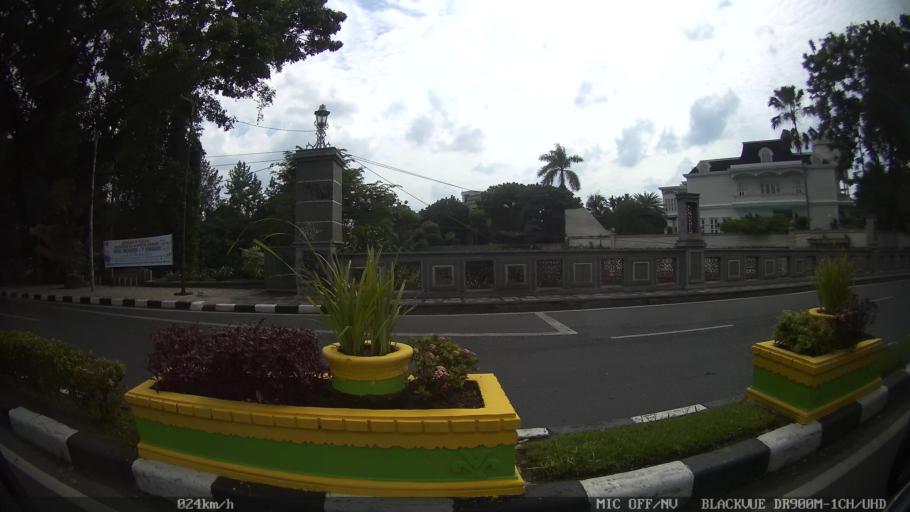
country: ID
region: North Sumatra
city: Medan
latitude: 3.5767
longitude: 98.6681
